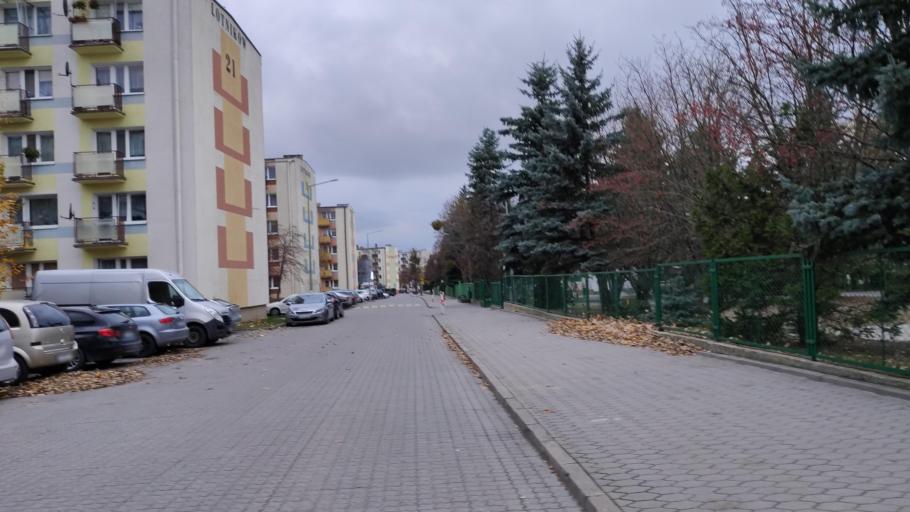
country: PL
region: Kujawsko-Pomorskie
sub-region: Powiat zninski
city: Barcin
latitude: 52.8535
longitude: 17.9440
